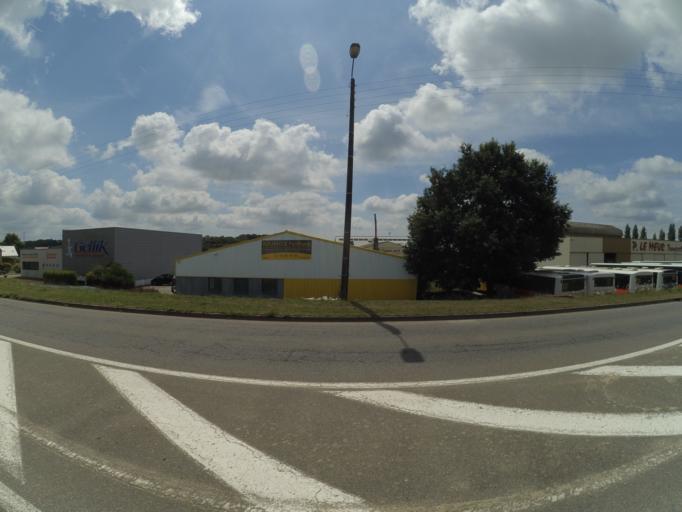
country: FR
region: Brittany
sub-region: Departement du Finistere
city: Rosporden
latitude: 47.9641
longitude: -3.8493
